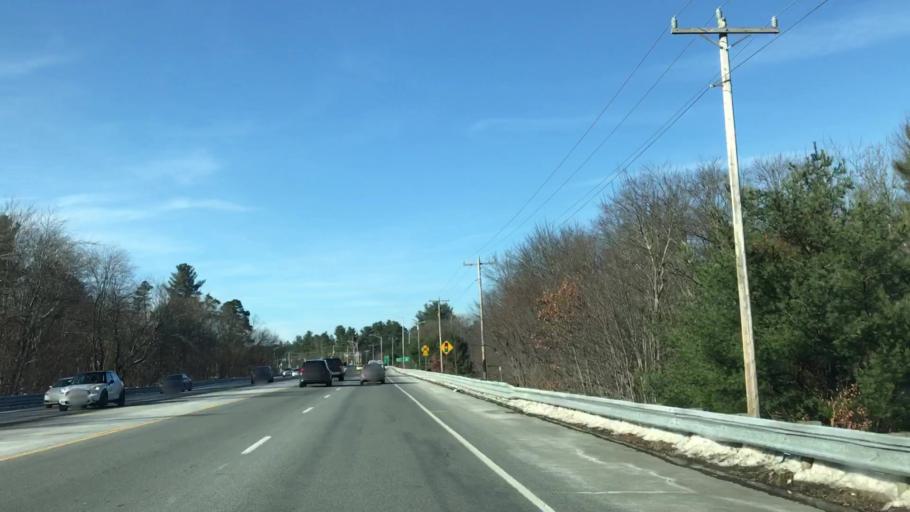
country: US
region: New Hampshire
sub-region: Hillsborough County
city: Milford
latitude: 42.8194
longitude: -71.6032
